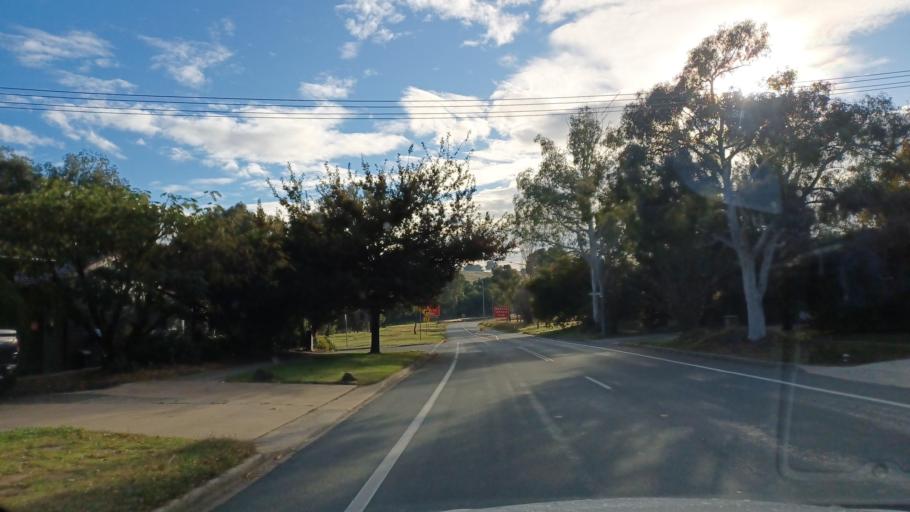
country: AU
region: Australian Capital Territory
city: Belconnen
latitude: -35.1890
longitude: 149.0472
